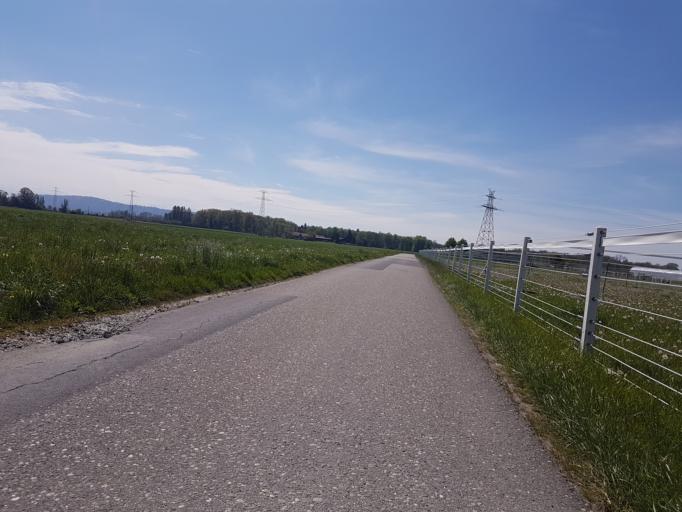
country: CH
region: Neuchatel
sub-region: Neuchatel District
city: Cornaux
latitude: 47.0186
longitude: 7.0363
